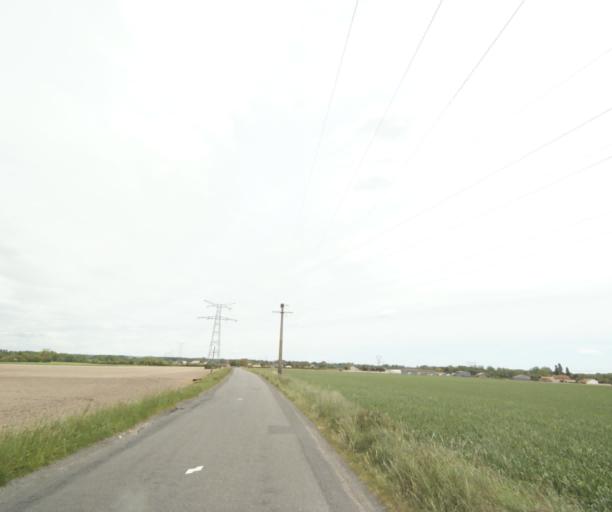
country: FR
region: Poitou-Charentes
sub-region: Departement de la Charente-Maritime
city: Les Gonds
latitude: 45.6906
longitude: -0.6040
